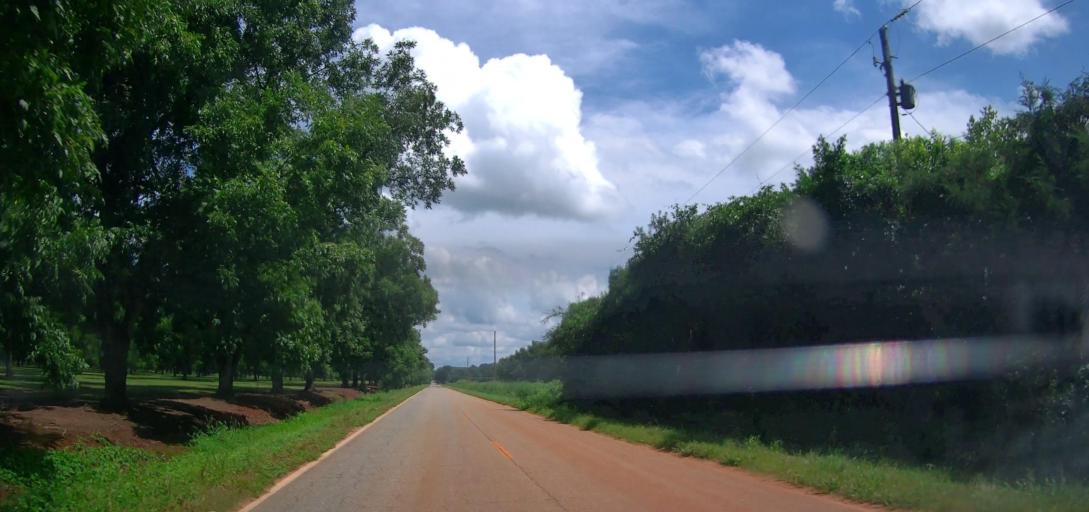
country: US
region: Georgia
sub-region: Houston County
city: Perry
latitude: 32.5212
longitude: -83.7870
